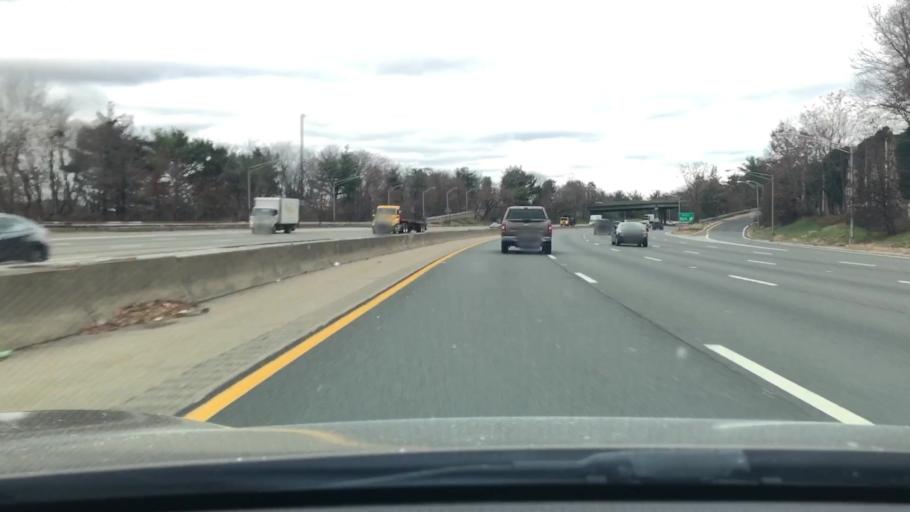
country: US
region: New Jersey
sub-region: Passaic County
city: Woodland Park
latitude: 40.9022
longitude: -74.1958
